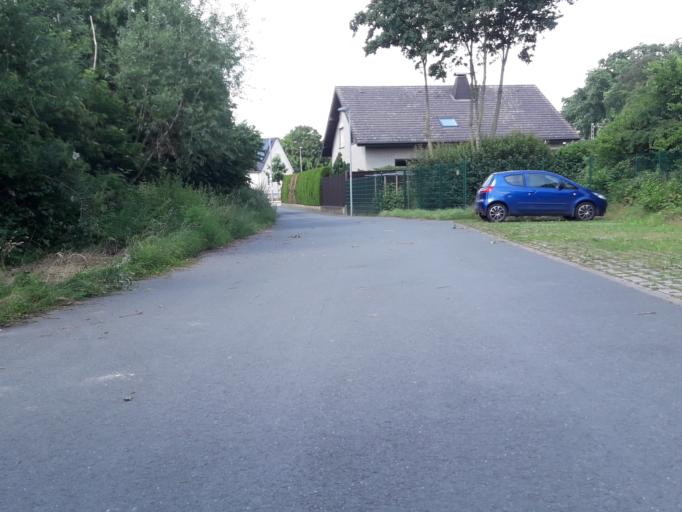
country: DE
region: North Rhine-Westphalia
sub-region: Regierungsbezirk Detmold
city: Salzkotten
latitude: 51.7111
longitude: 8.6442
